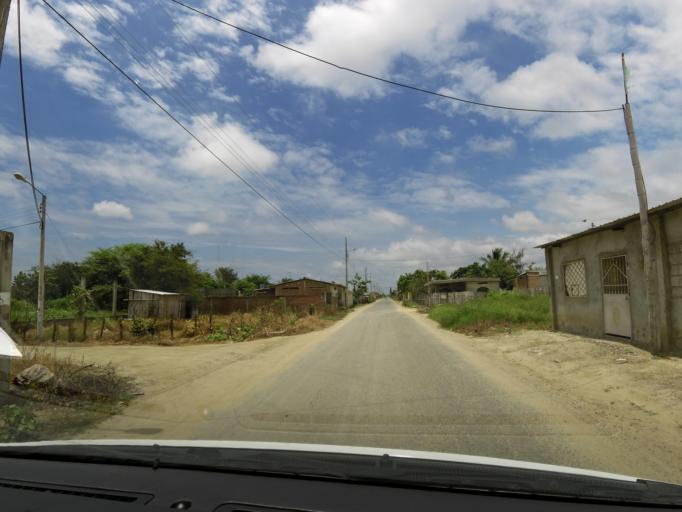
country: EC
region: El Oro
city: Huaquillas
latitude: -3.4864
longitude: -80.2106
